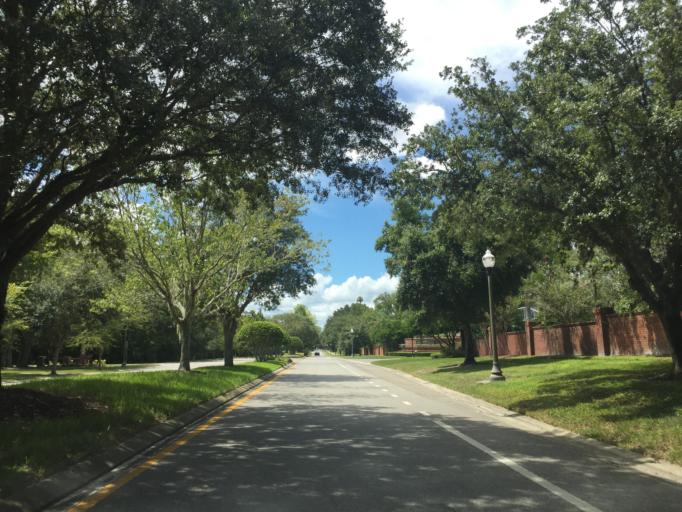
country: US
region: Florida
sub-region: Seminole County
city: Oviedo
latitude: 28.6767
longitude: -81.2411
